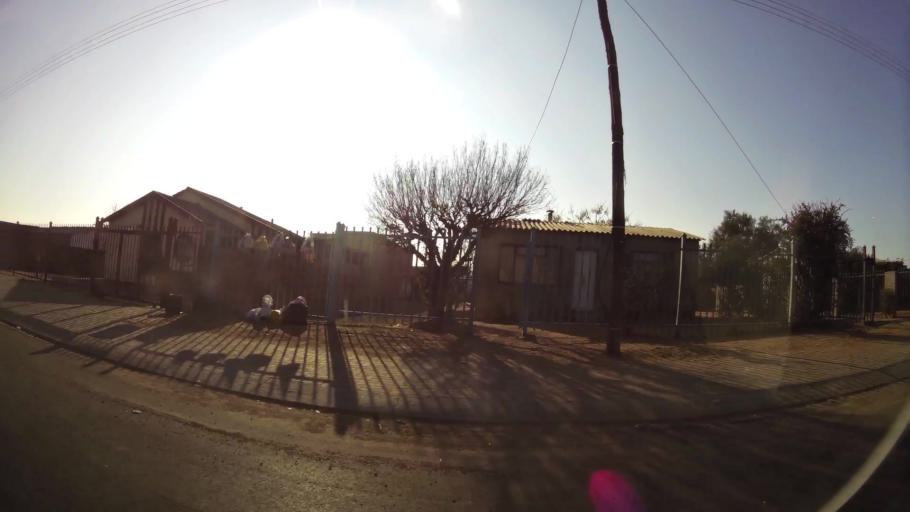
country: ZA
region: Orange Free State
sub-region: Mangaung Metropolitan Municipality
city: Bloemfontein
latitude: -29.1542
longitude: 26.2533
